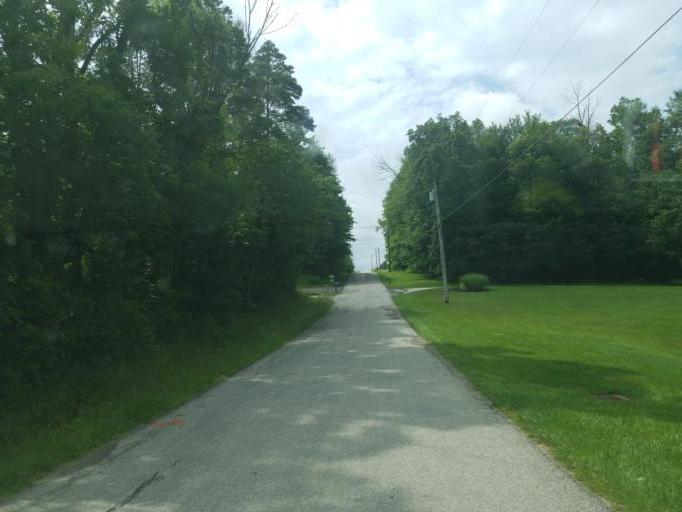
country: US
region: Ohio
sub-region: Richland County
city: Ontario
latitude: 40.7270
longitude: -82.6269
